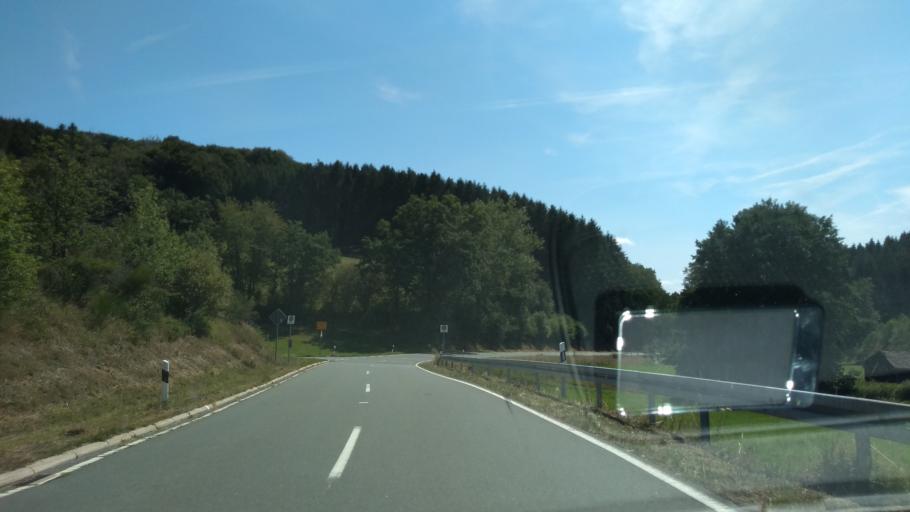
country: DE
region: North Rhine-Westphalia
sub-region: Regierungsbezirk Arnsberg
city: Drolshagen
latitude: 51.0906
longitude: 7.7872
